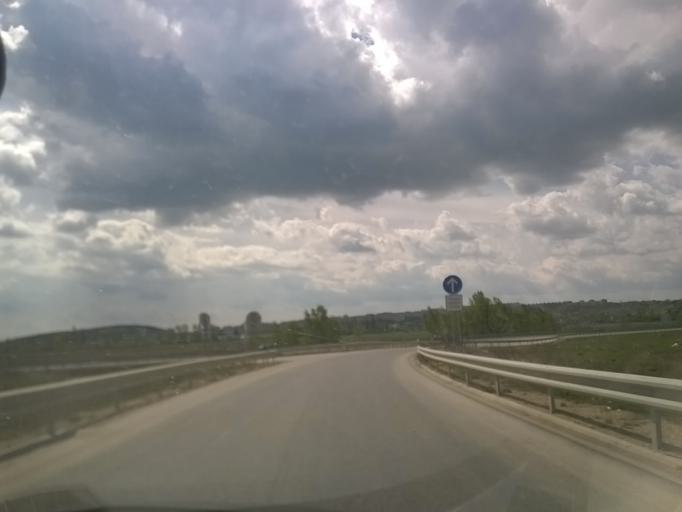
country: SK
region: Nitriansky
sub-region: Okres Nitra
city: Nitra
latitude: 48.3263
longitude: 18.0617
